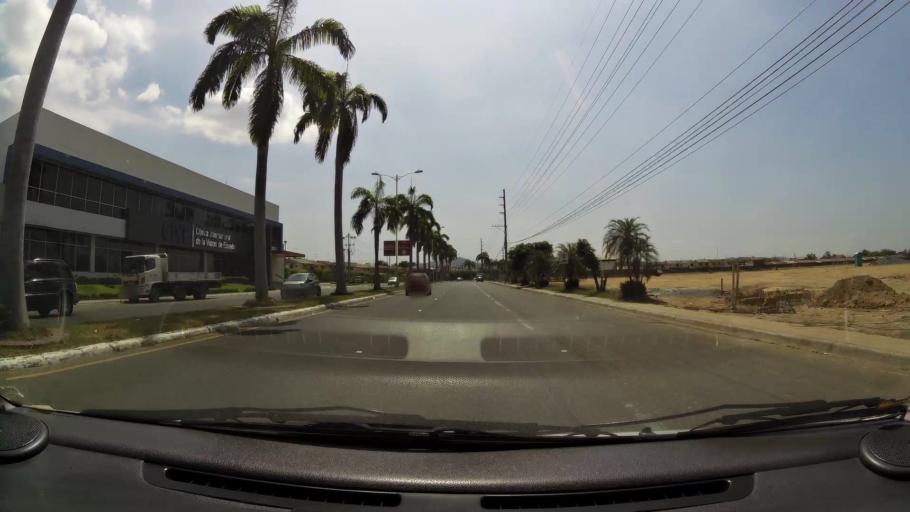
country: EC
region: Guayas
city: Eloy Alfaro
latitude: -2.0485
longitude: -79.8902
